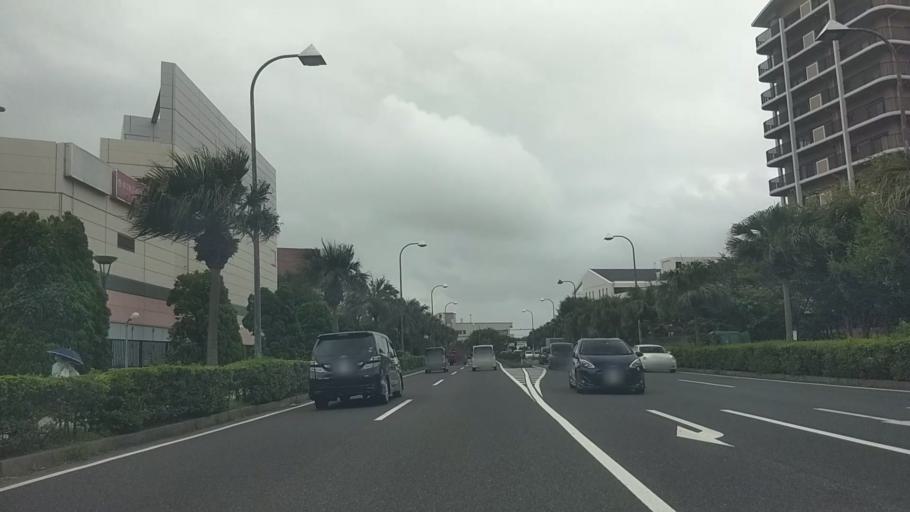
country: JP
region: Kanagawa
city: Yokosuka
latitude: 35.2725
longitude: 139.6841
